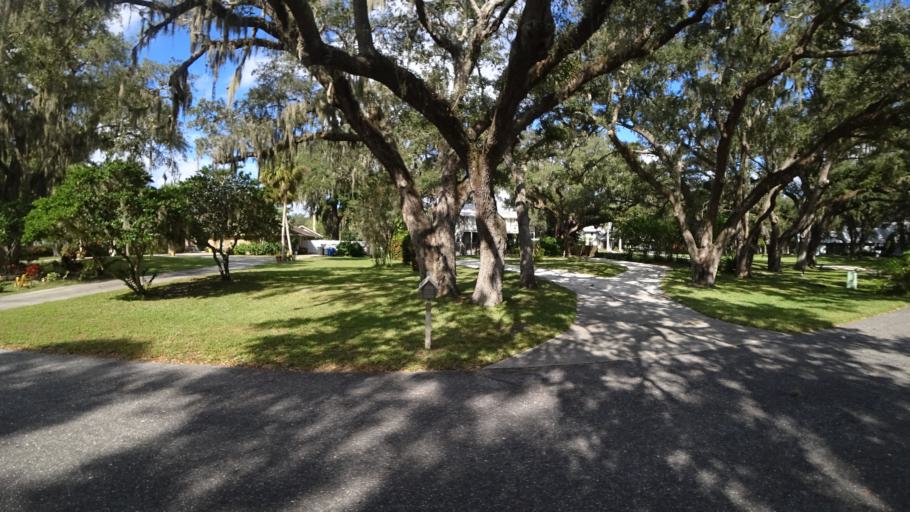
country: US
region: Florida
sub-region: Sarasota County
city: North Sarasota
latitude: 27.4098
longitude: -82.5042
